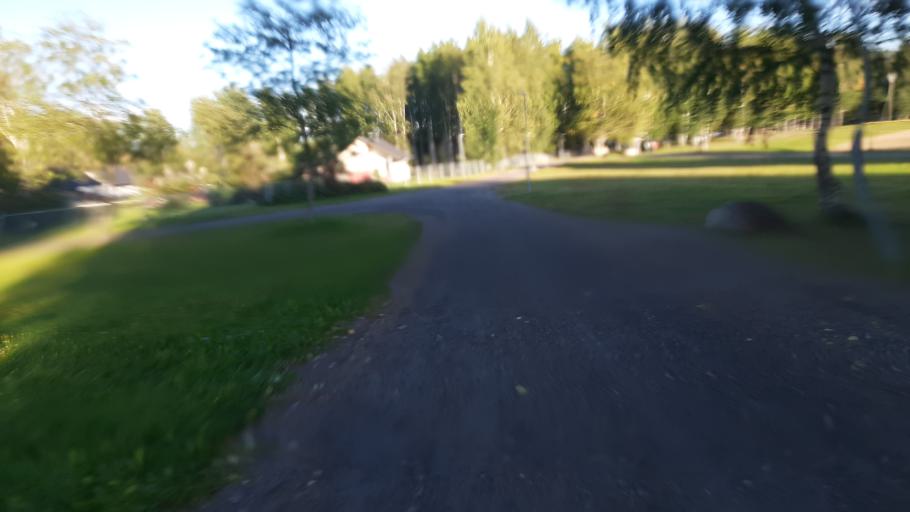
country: FI
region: North Karelia
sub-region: Joensuu
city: Joensuu
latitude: 62.5958
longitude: 29.7377
